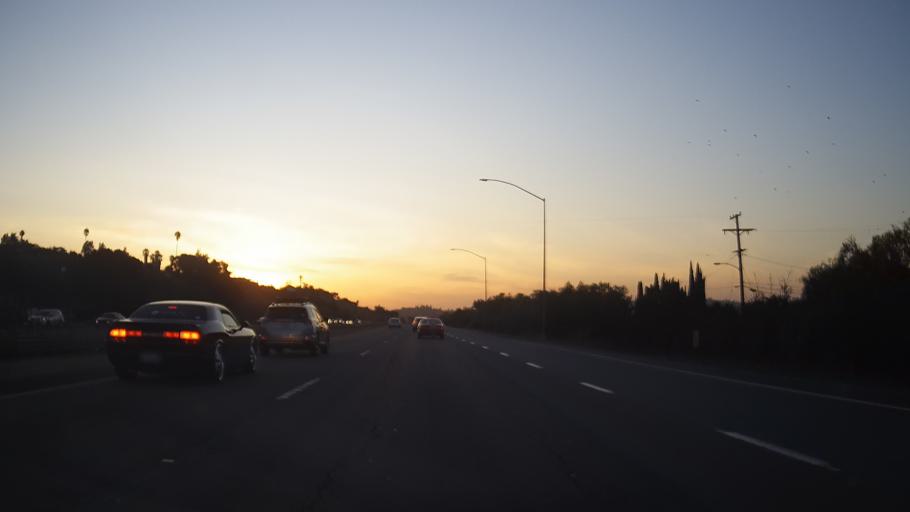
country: US
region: California
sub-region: San Diego County
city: Casa de Oro-Mount Helix
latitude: 32.7449
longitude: -116.9665
